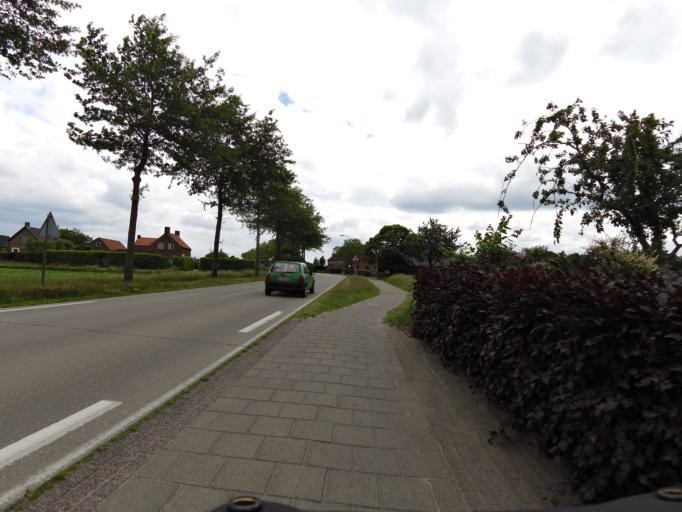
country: BE
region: Flanders
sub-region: Provincie Antwerpen
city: Baarle-Hertog
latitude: 51.4545
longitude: 4.8673
